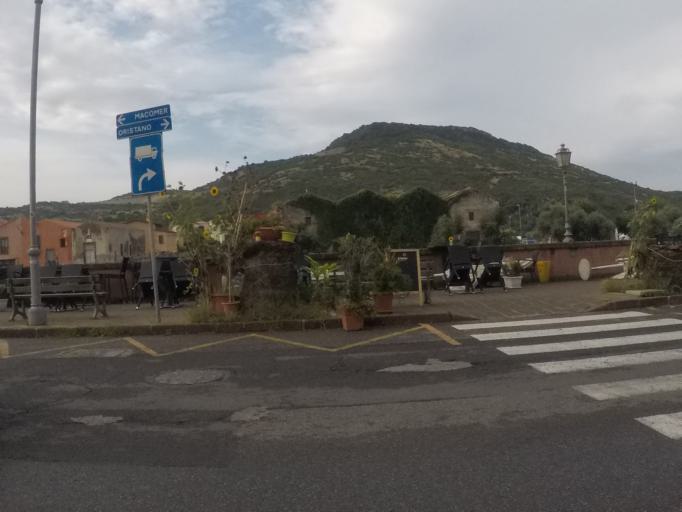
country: IT
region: Sardinia
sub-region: Provincia di Oristano
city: Bosa
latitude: 40.2955
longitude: 8.5000
